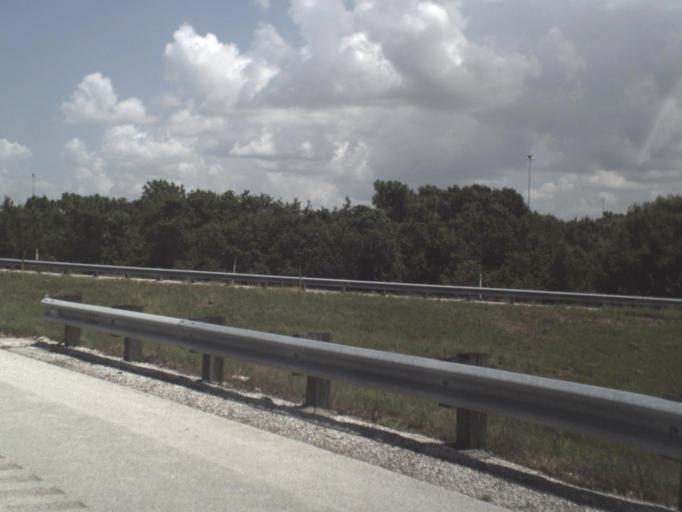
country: US
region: Florida
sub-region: Hillsborough County
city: Sun City Center
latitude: 27.7113
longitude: -82.3851
